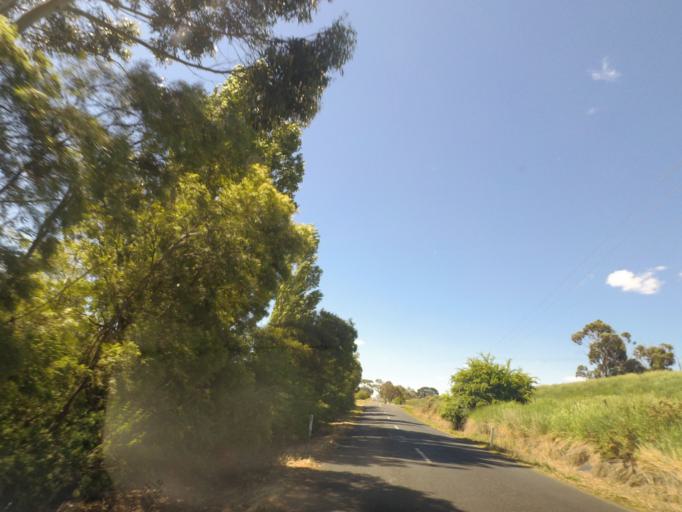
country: AU
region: Victoria
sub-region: Mount Alexander
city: Castlemaine
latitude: -37.2873
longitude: 144.4464
